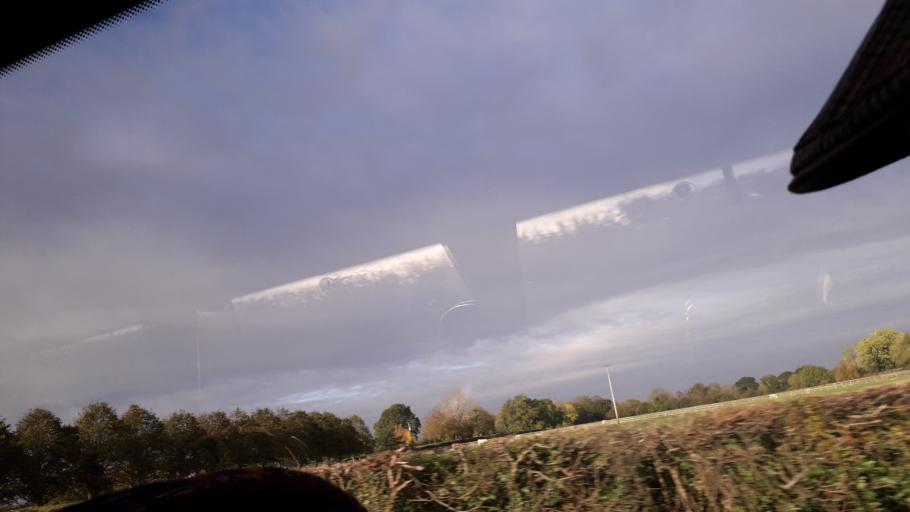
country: IE
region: Leinster
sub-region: Kildare
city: Maynooth
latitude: 53.3577
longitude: -6.5942
